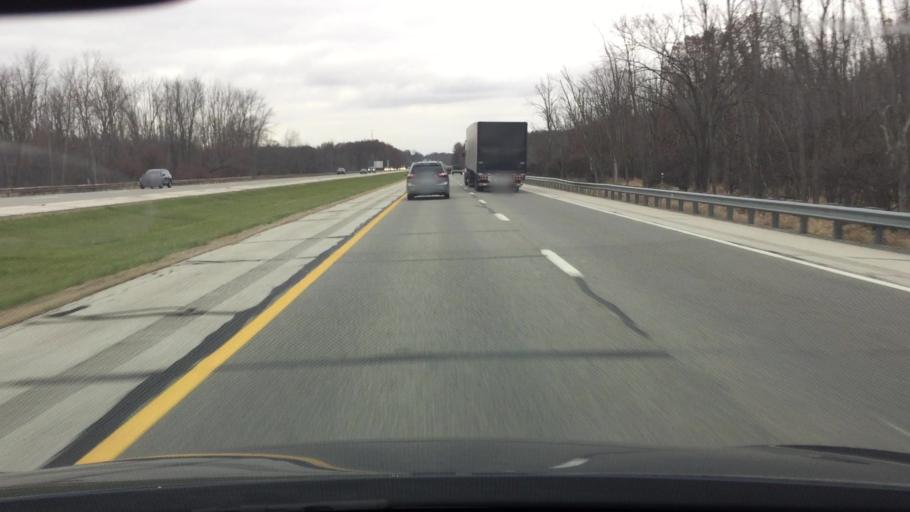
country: US
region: Ohio
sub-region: Mahoning County
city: Boardman
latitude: 40.9976
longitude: -80.6958
